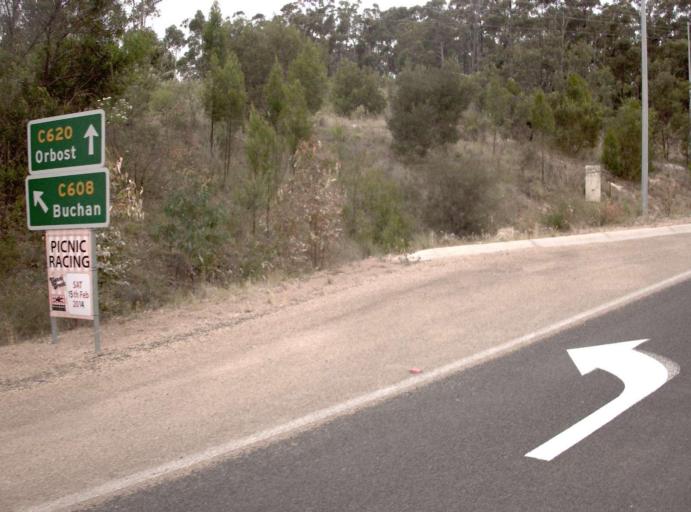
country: AU
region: Victoria
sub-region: East Gippsland
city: Lakes Entrance
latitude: -37.6917
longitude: 148.0407
